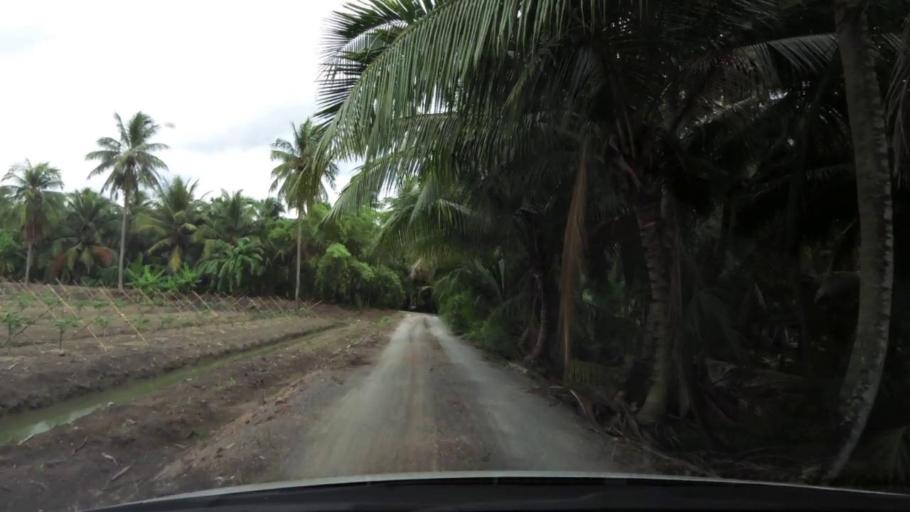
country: TH
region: Ratchaburi
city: Damnoen Saduak
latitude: 13.5547
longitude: 99.9873
